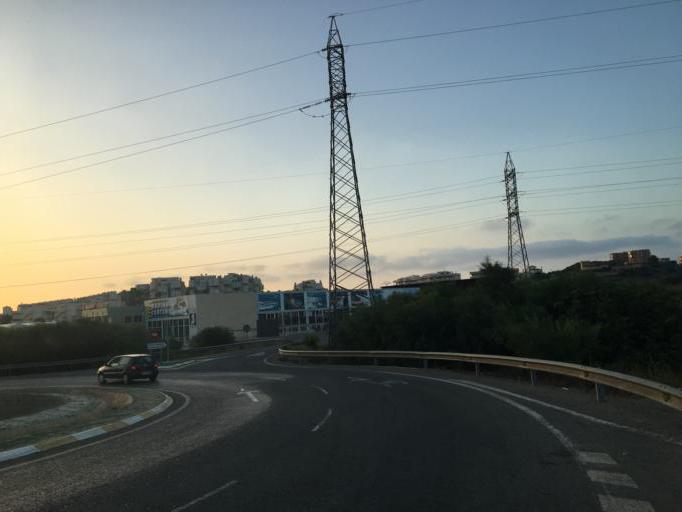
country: ES
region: Murcia
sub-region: Murcia
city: La Manga del Mar Menor
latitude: 37.6276
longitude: -0.7144
